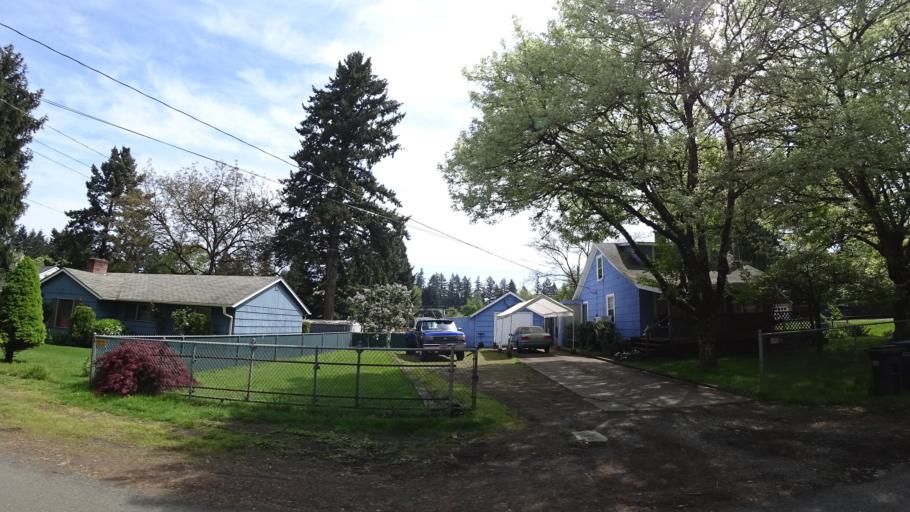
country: US
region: Oregon
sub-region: Clackamas County
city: Oatfield
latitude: 45.4501
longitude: -122.6009
